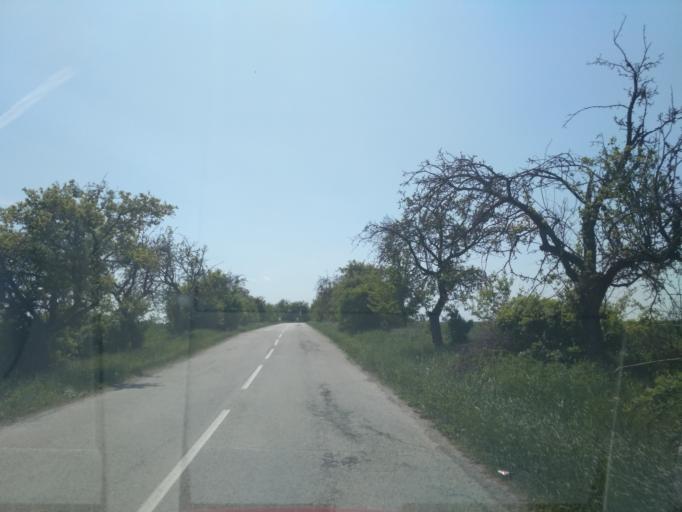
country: SK
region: Kosicky
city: Kosice
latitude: 48.8059
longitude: 21.3993
